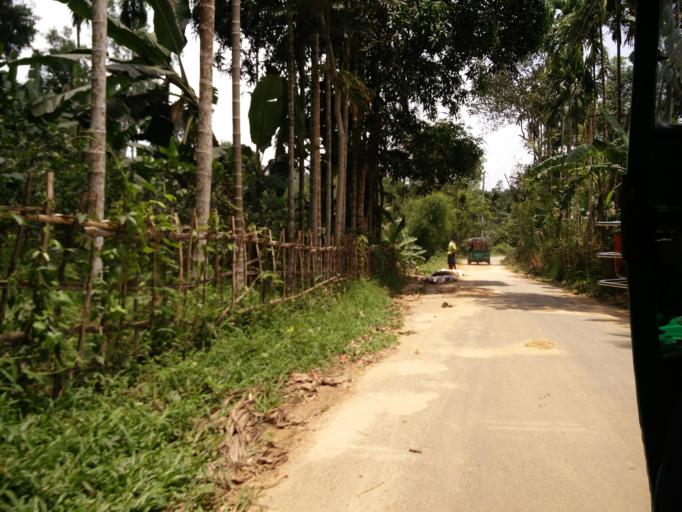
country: IN
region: Tripura
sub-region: Dhalai
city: Kamalpur
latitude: 24.3029
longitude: 91.7841
